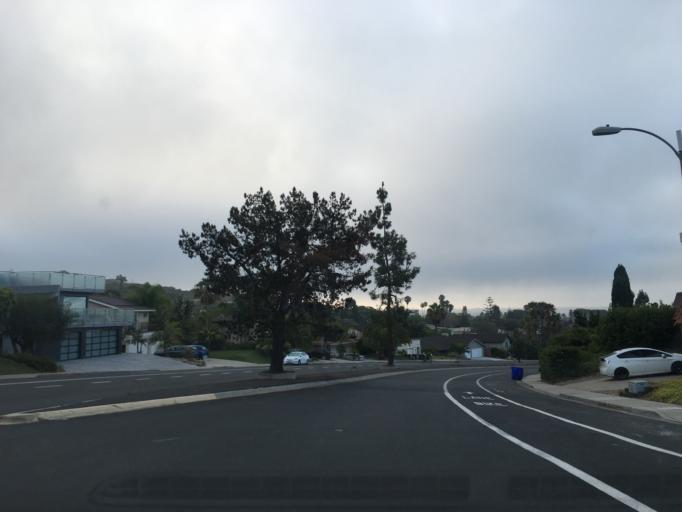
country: US
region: California
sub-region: San Diego County
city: La Jolla
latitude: 32.8151
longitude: -117.2344
